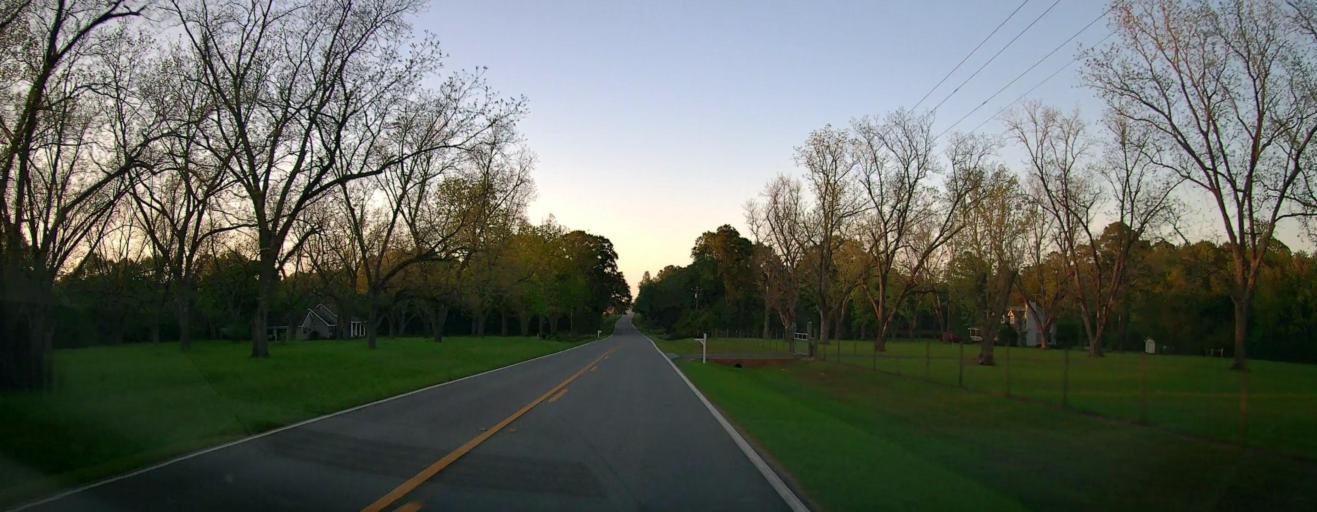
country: US
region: Georgia
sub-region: Ben Hill County
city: Fitzgerald
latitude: 31.7203
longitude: -83.3099
